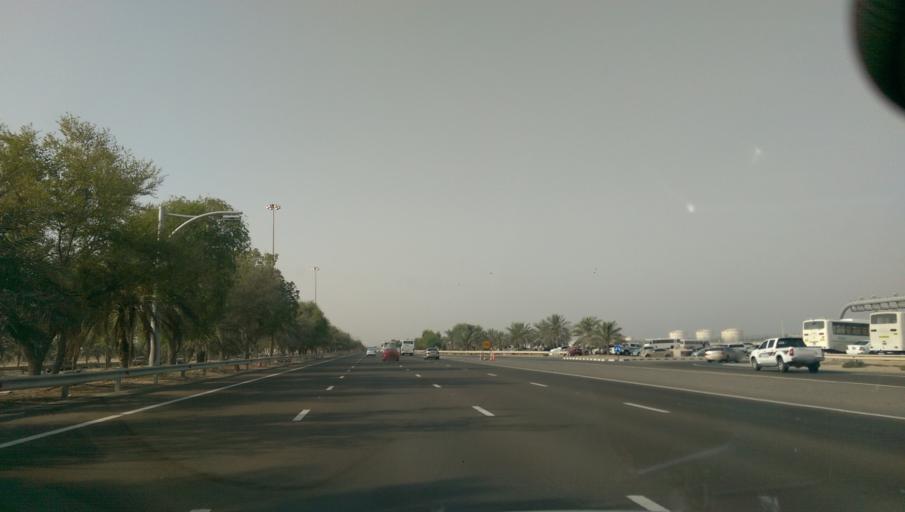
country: AE
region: Abu Dhabi
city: Abu Dhabi
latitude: 24.4430
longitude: 54.6783
